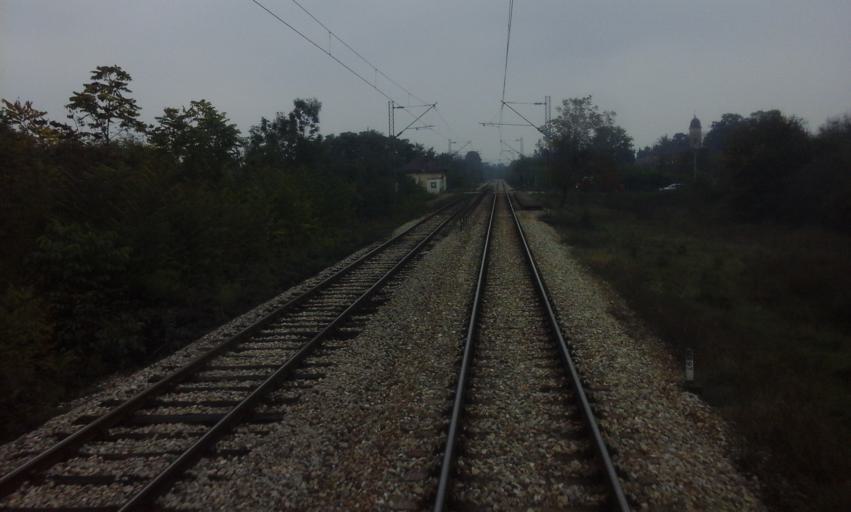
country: RS
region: Central Serbia
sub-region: Podunavski Okrug
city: Velika Plana
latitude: 44.2631
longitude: 21.0917
